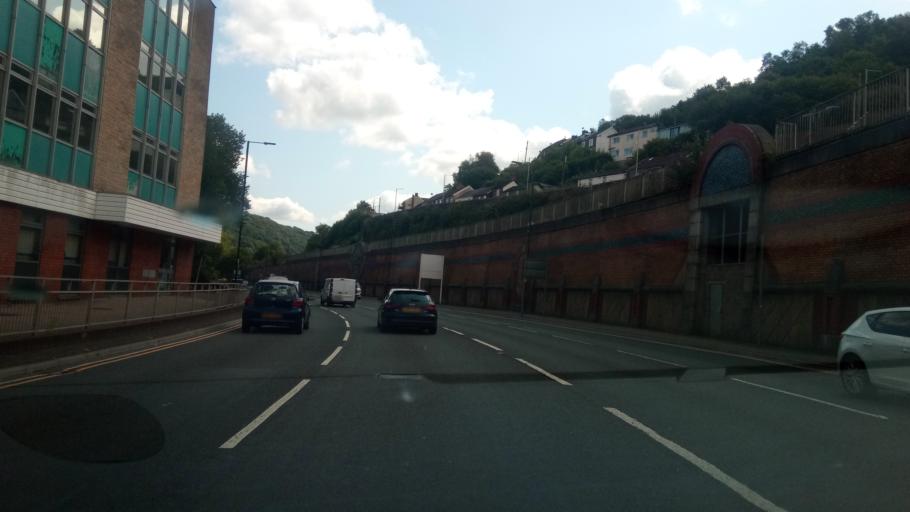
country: GB
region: Wales
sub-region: Rhondda Cynon Taf
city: Pontypridd
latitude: 51.5988
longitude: -3.3399
